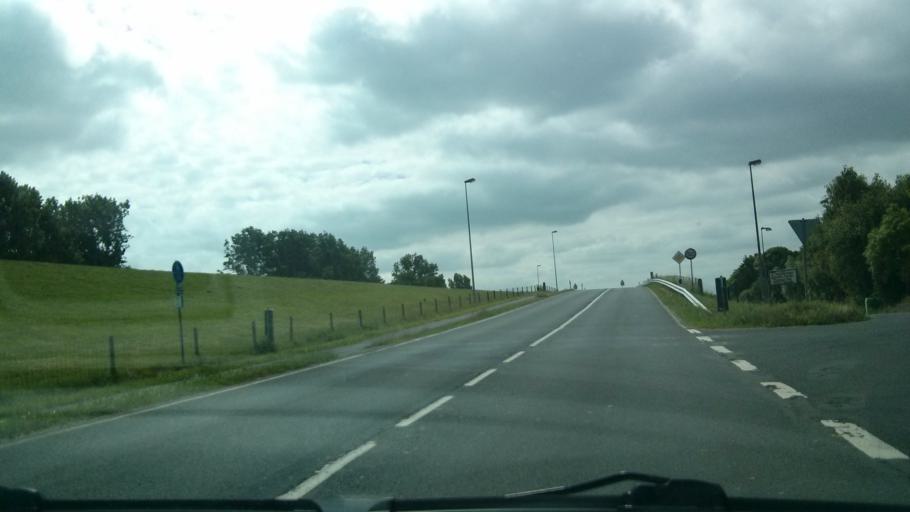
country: DE
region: Lower Saxony
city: Nordenham
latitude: 53.4442
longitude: 8.4765
